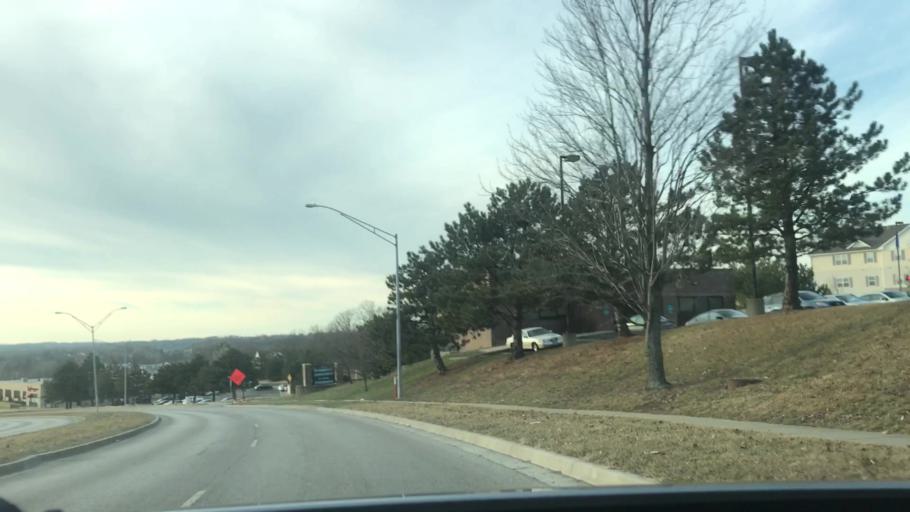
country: US
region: Missouri
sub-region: Clay County
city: Gladstone
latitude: 39.1970
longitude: -94.5822
